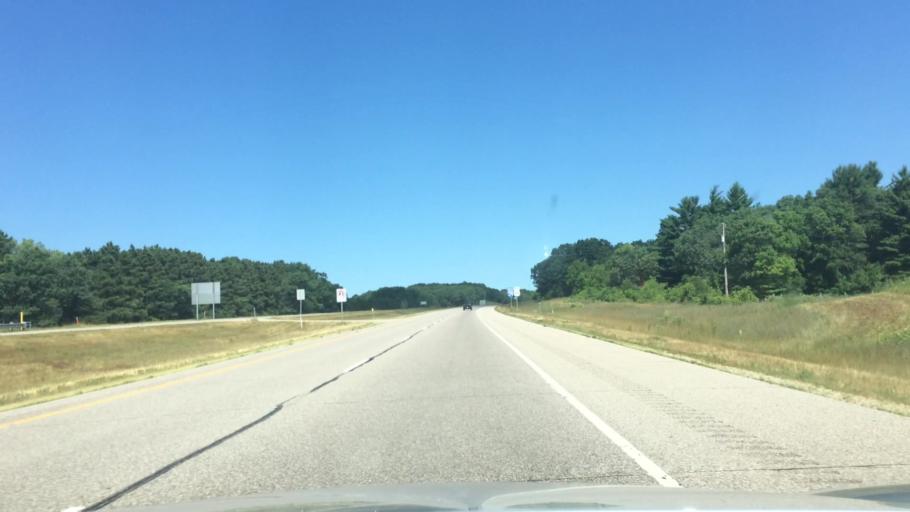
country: US
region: Wisconsin
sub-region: Marquette County
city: Westfield
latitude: 44.0410
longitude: -89.5341
